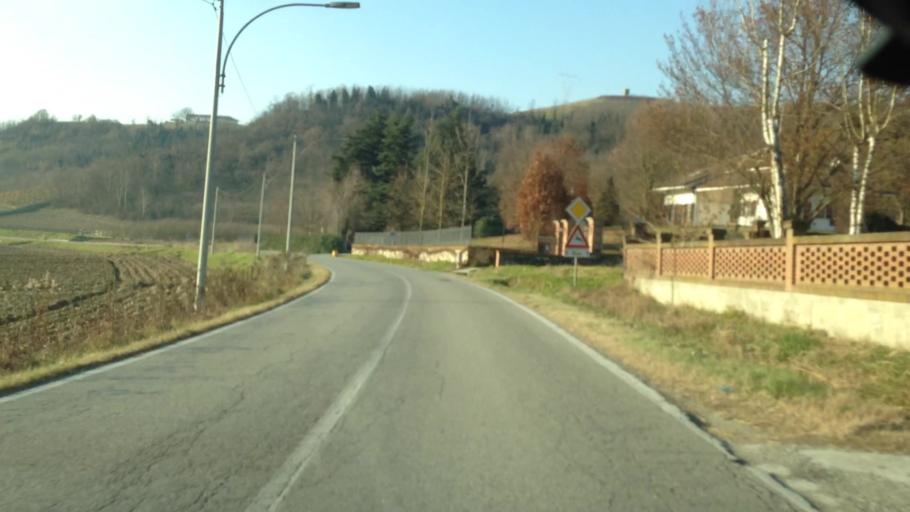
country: IT
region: Piedmont
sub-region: Provincia di Asti
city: Belveglio
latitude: 44.8303
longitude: 8.3230
